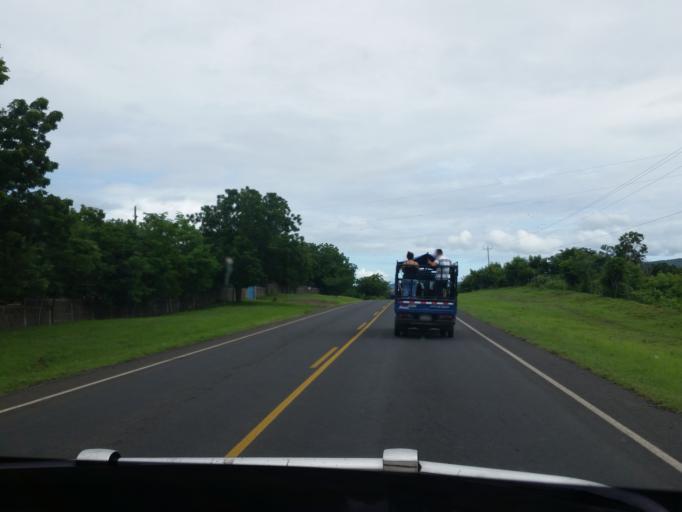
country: NI
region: Managua
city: Tipitapa
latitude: 12.3799
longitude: -86.0457
